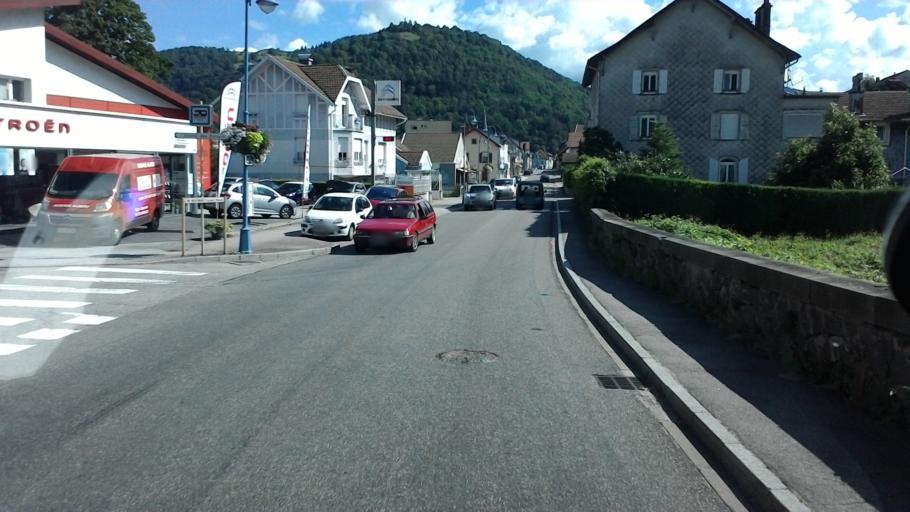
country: FR
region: Lorraine
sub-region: Departement des Vosges
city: Cornimont
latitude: 47.9590
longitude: 6.8318
